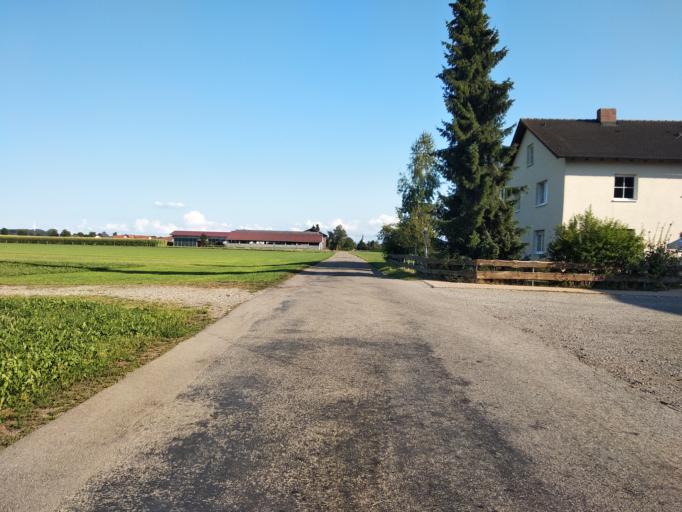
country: DE
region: Bavaria
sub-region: Swabia
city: Legau
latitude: 47.8674
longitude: 10.1200
